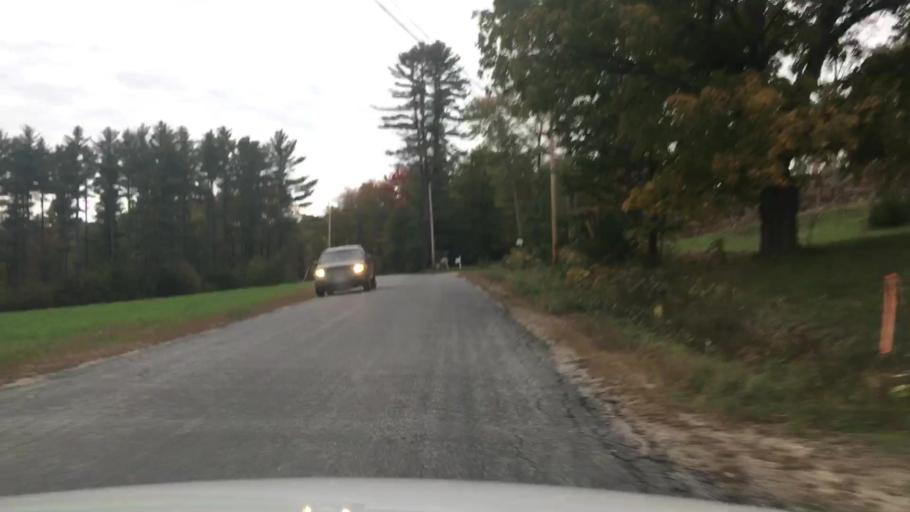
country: US
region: Maine
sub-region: Oxford County
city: Bethel
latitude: 44.4700
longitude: -70.7839
